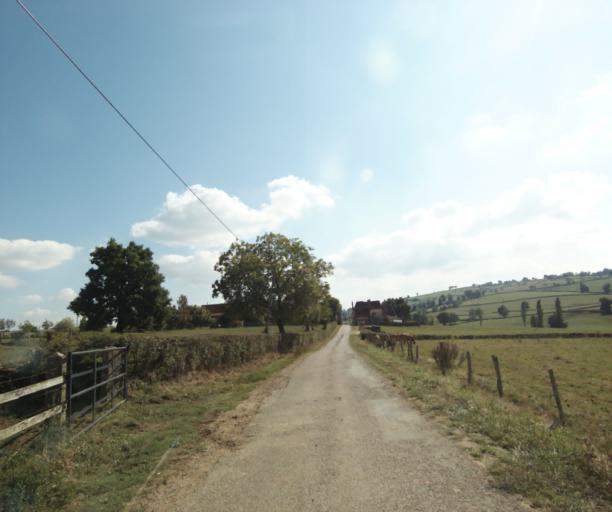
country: FR
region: Bourgogne
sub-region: Departement de Saone-et-Loire
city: Charolles
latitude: 46.3743
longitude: 4.2242
